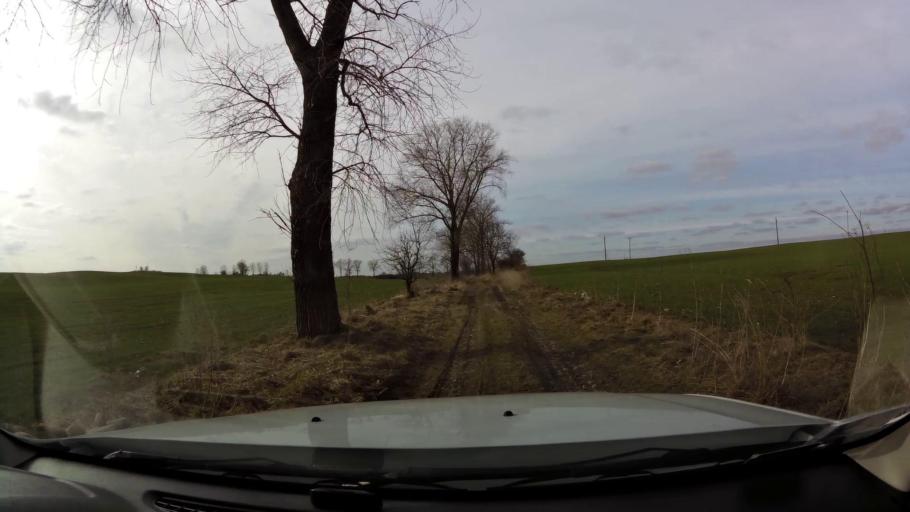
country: PL
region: West Pomeranian Voivodeship
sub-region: Powiat drawski
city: Drawsko Pomorskie
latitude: 53.5230
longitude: 15.7668
